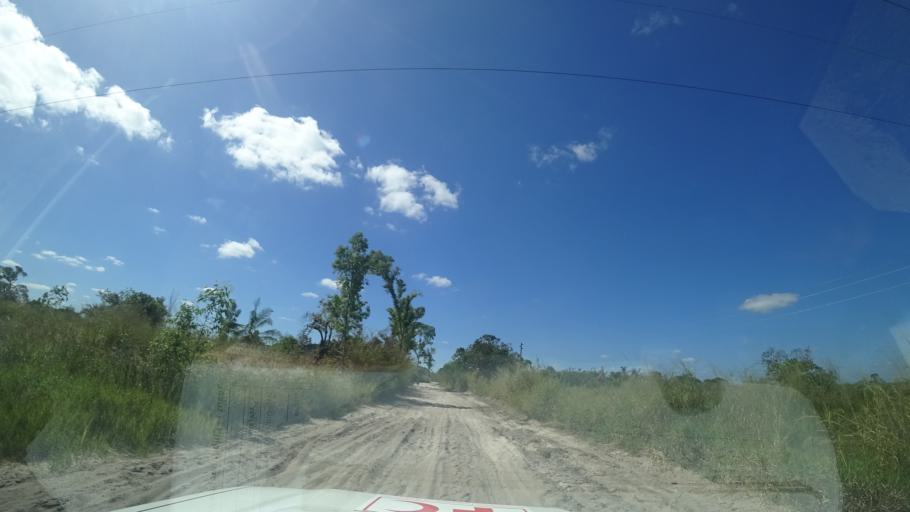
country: MZ
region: Sofala
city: Dondo
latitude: -19.5054
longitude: 34.6106
